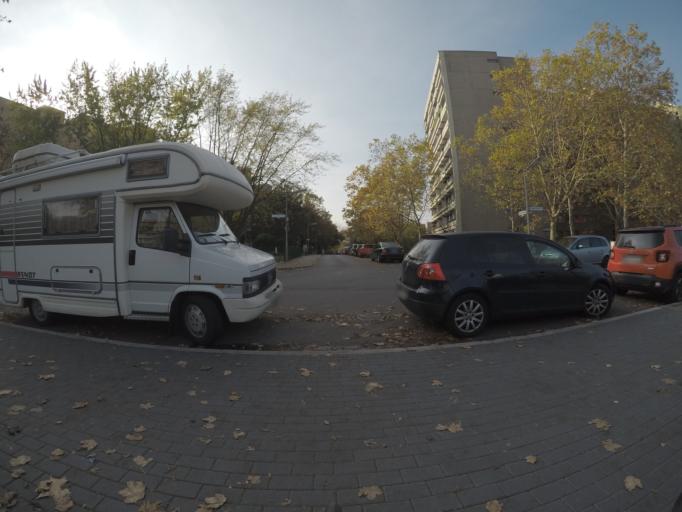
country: DE
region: Berlin
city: Britz
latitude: 52.4183
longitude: 13.4352
